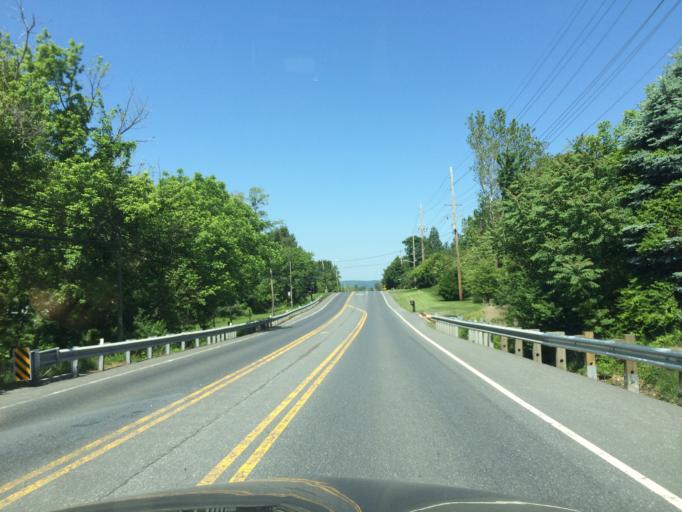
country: US
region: Maryland
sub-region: Frederick County
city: Braddock Heights
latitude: 39.4311
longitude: -77.5097
